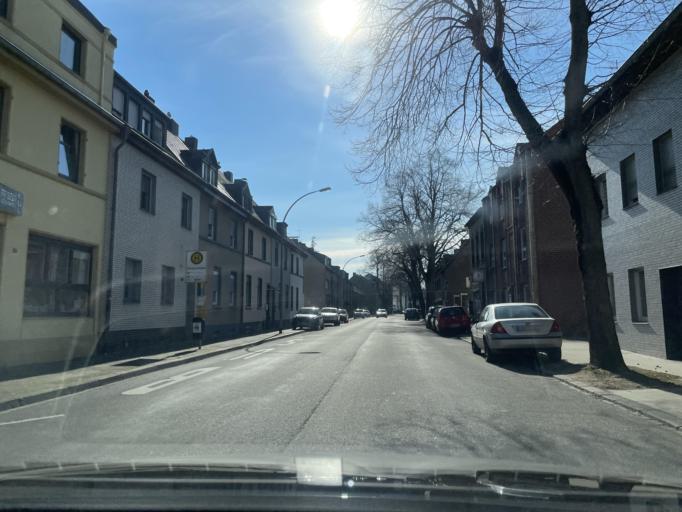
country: DE
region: North Rhine-Westphalia
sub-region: Regierungsbezirk Dusseldorf
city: Monchengladbach
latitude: 51.2209
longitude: 6.4543
